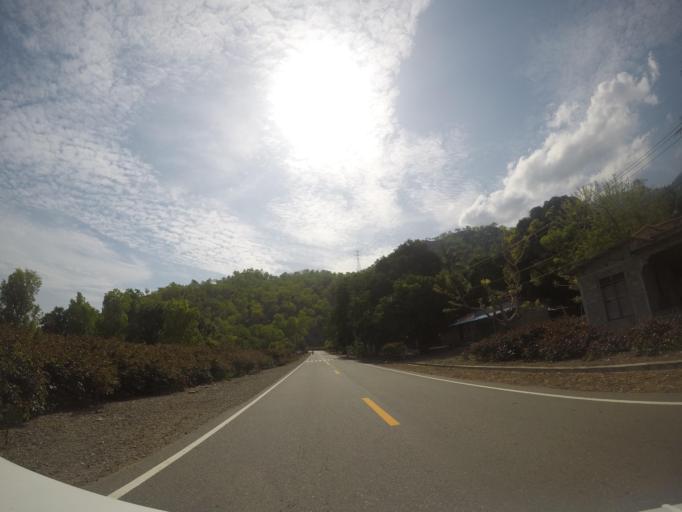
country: TL
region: Manatuto
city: Manatuto
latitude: -8.4785
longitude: 125.8905
